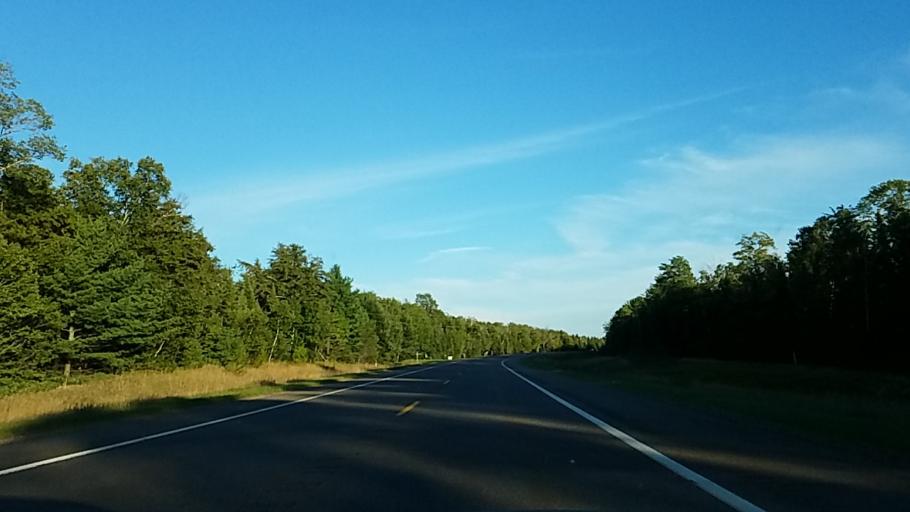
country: US
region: Michigan
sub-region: Alger County
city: Munising
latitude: 46.4614
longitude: -86.8973
